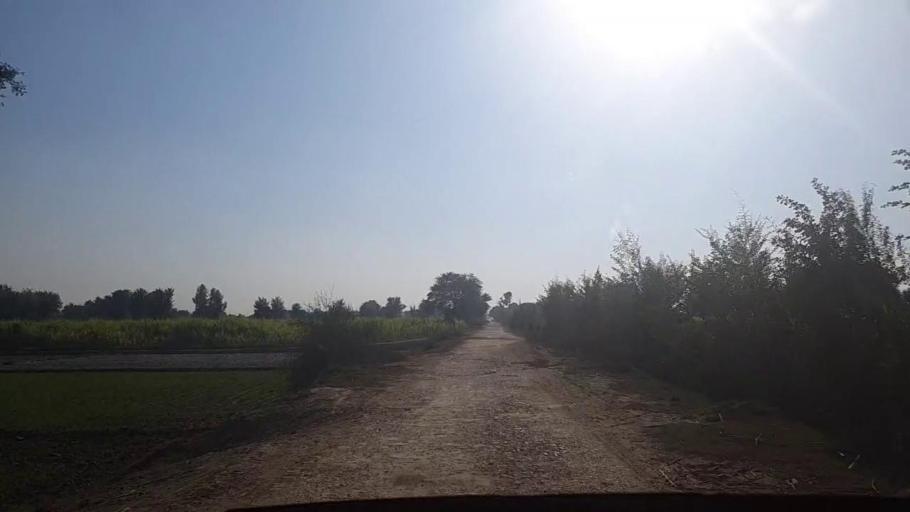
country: PK
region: Sindh
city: Gambat
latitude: 27.3697
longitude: 68.4629
